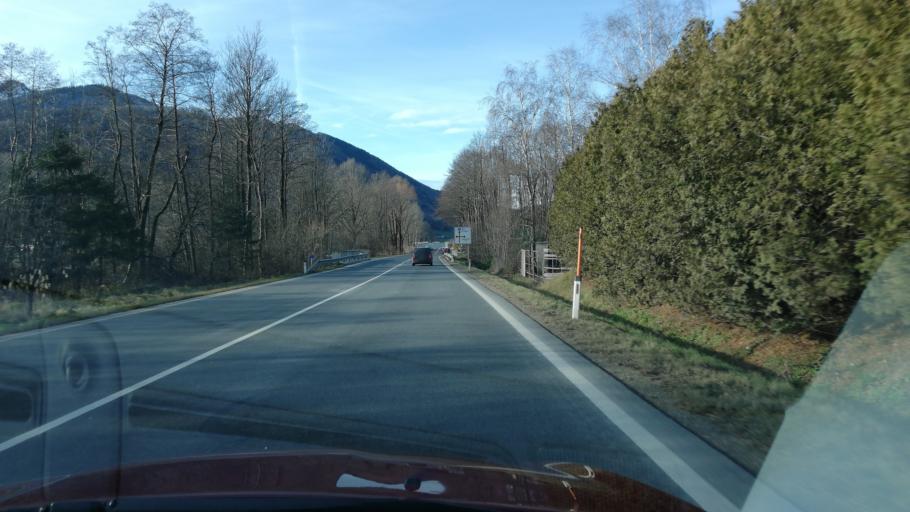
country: AT
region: Upper Austria
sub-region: Politischer Bezirk Kirchdorf an der Krems
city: Micheldorf in Oberoesterreich
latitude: 47.8691
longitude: 14.1406
